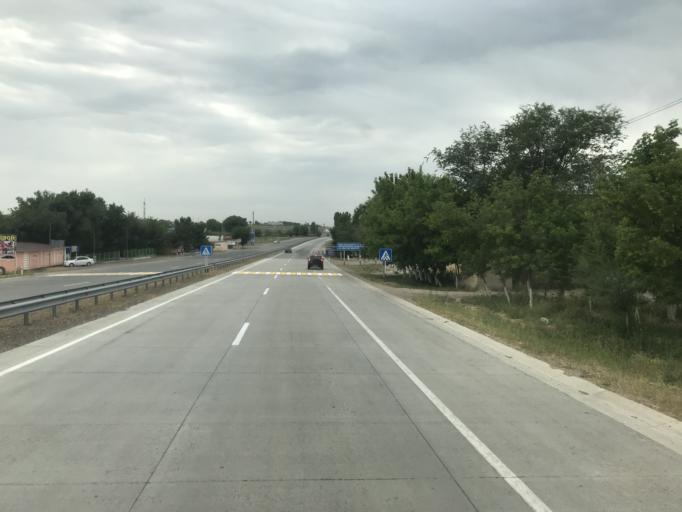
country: UZ
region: Toshkent
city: Salor
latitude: 41.5057
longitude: 69.3725
